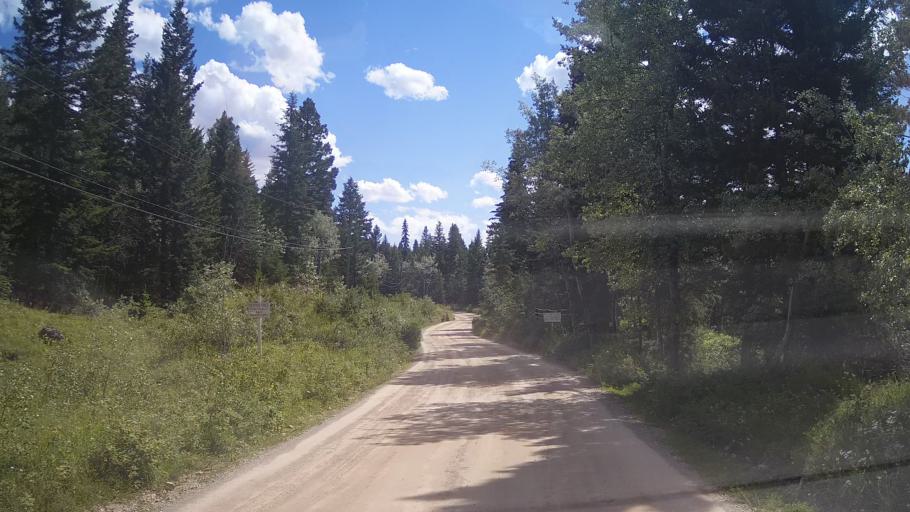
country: CA
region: British Columbia
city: Lillooet
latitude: 51.2820
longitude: -121.9675
